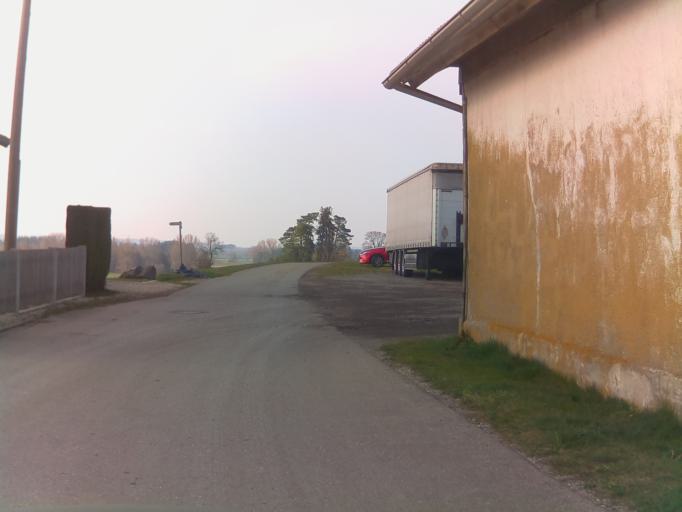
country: DE
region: Bavaria
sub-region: Swabia
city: Rieden
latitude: 47.9559
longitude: 10.6510
